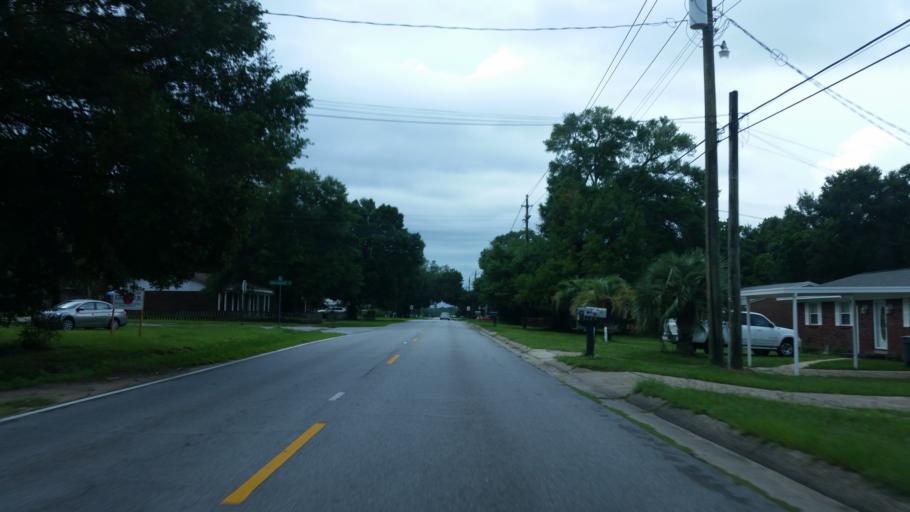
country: US
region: Florida
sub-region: Escambia County
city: Bellview
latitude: 30.4440
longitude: -87.3107
